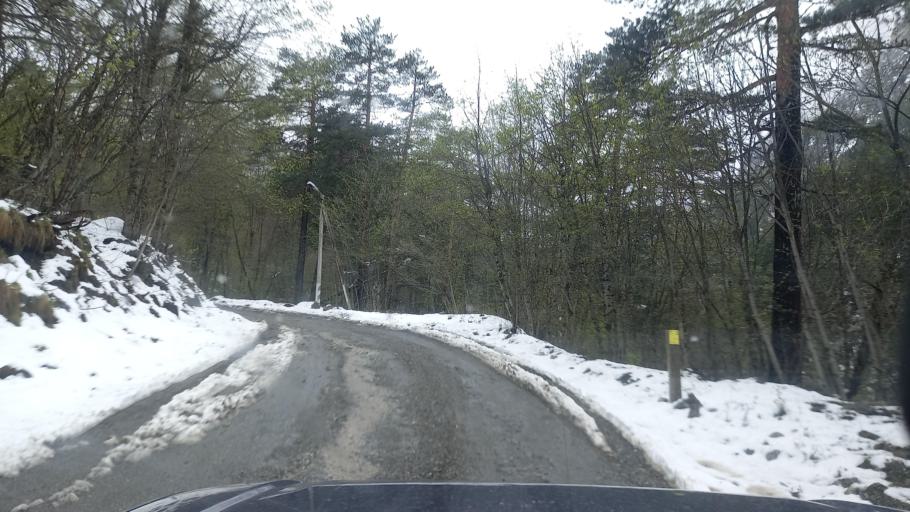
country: RU
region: North Ossetia
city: Mizur
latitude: 42.7900
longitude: 43.9094
